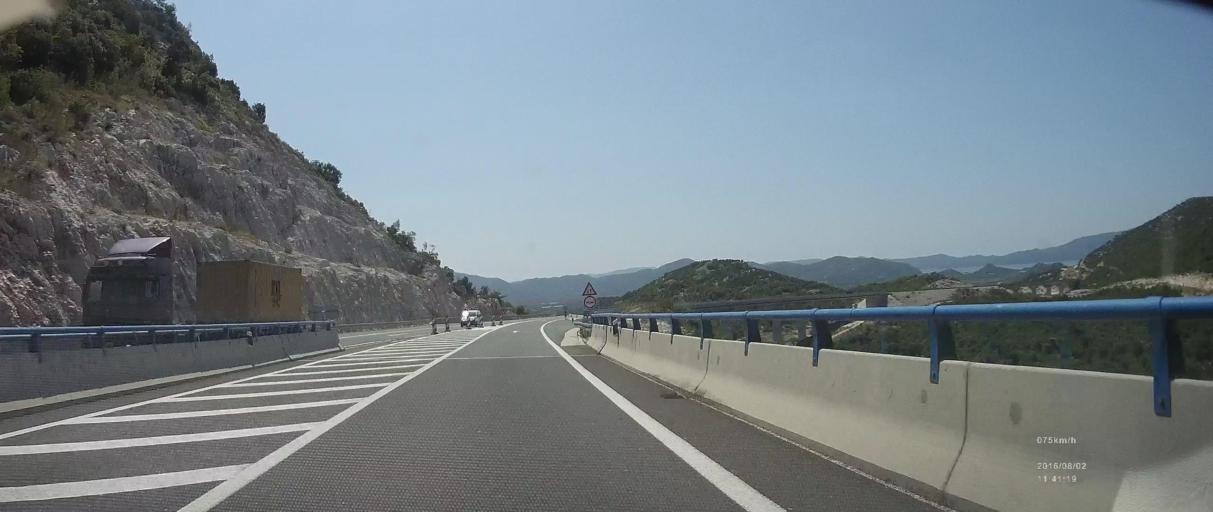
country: HR
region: Dubrovacko-Neretvanska
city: Komin
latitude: 43.0648
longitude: 17.4955
